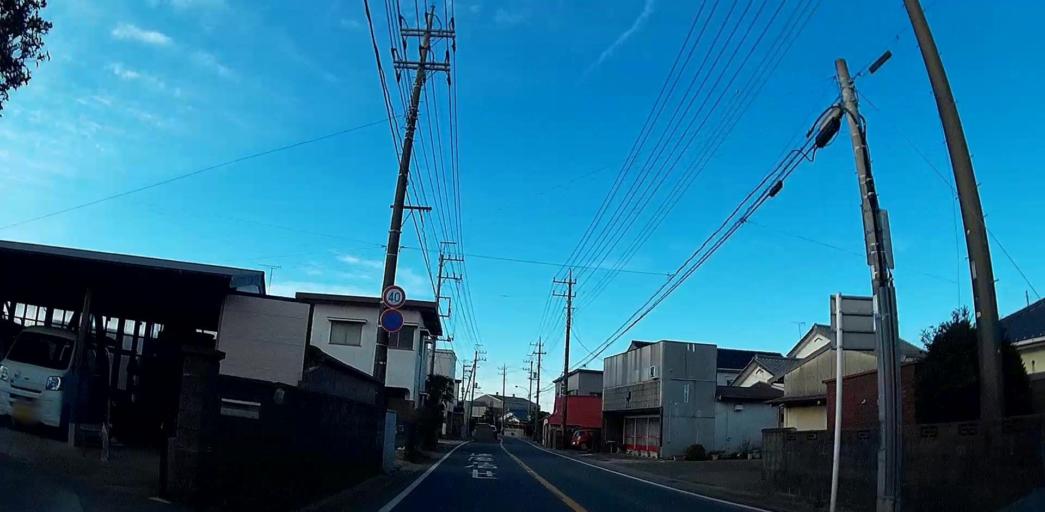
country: JP
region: Chiba
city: Omigawa
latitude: 35.8424
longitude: 140.6577
